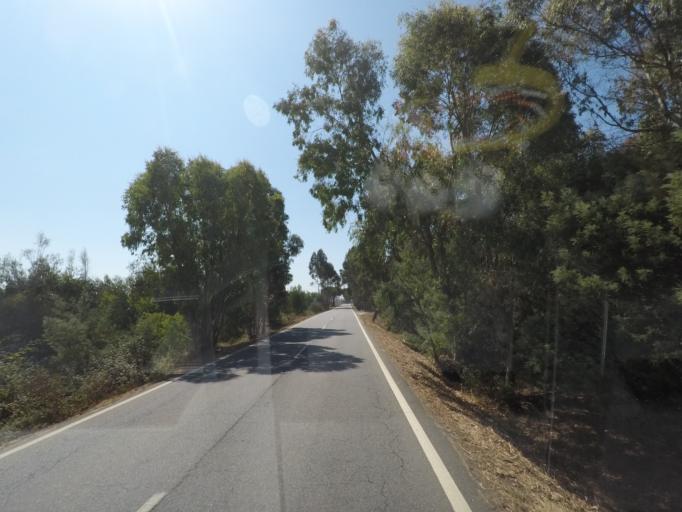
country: PT
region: Beja
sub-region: Odemira
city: Sao Teotonio
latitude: 37.5250
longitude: -8.7002
